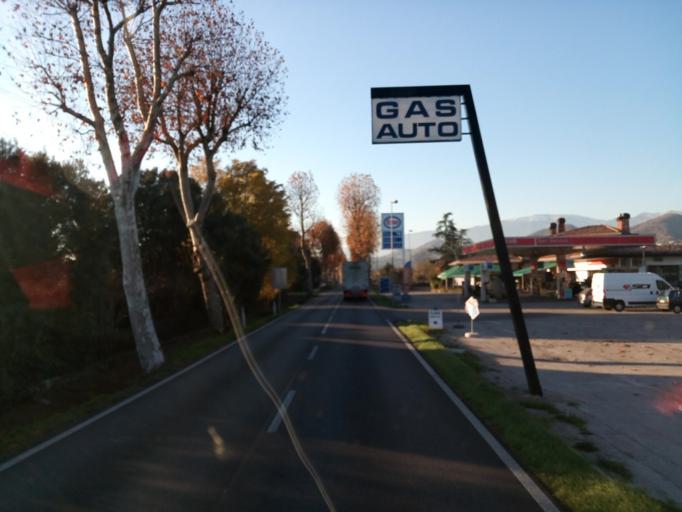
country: IT
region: Veneto
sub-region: Provincia di Treviso
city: Maser
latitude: 45.7928
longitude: 11.9731
